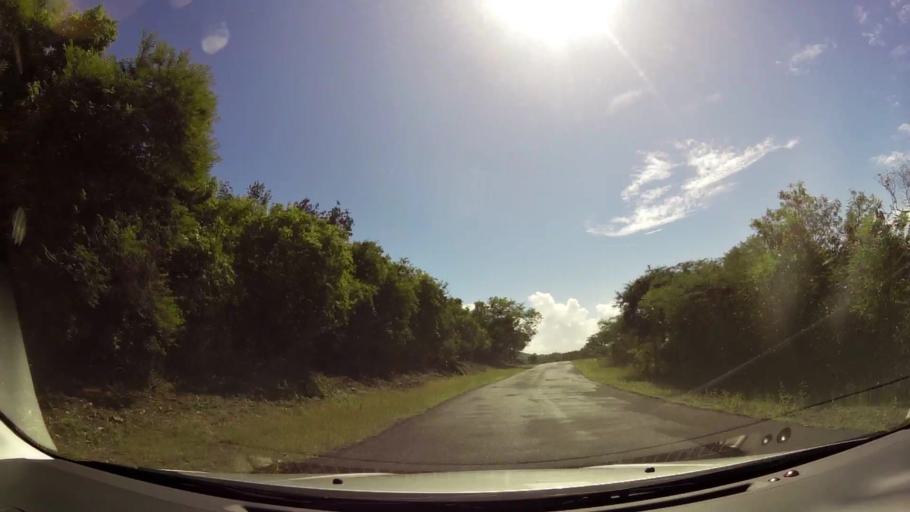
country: AG
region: Saint Paul
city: Falmouth
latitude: 17.0211
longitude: -61.7412
